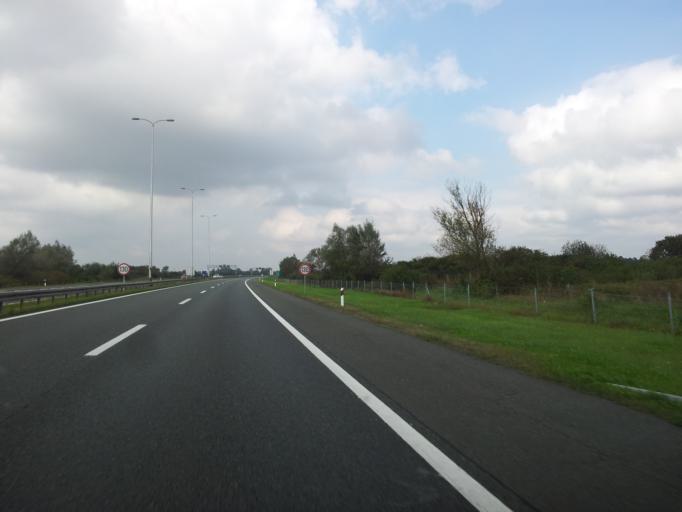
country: HR
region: Brodsko-Posavska
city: Okucani
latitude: 45.2308
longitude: 17.2074
